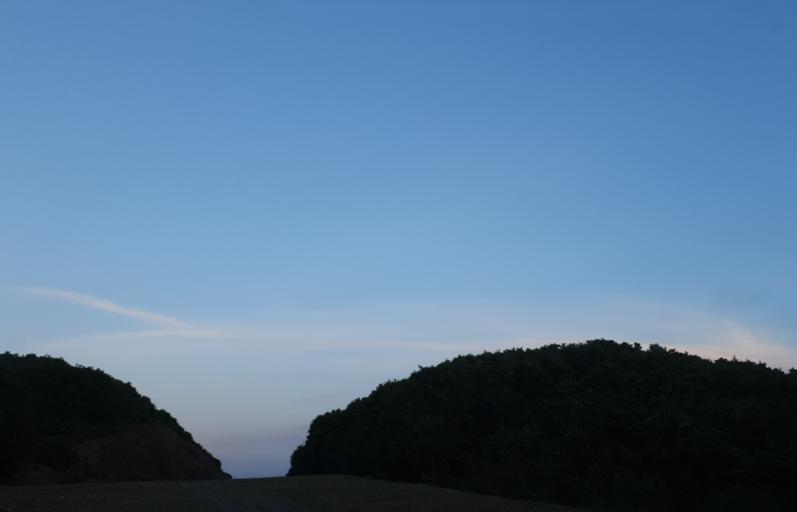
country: TR
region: Kirklareli
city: Salmydessus
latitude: 41.6882
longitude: 28.0809
